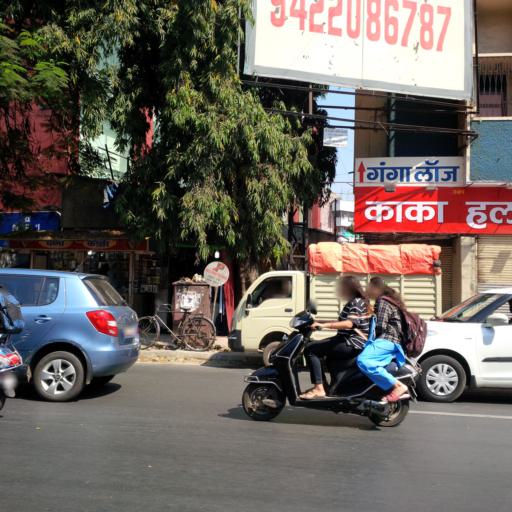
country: IN
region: Maharashtra
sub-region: Pune Division
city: Pune
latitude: 18.5163
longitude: 73.8421
